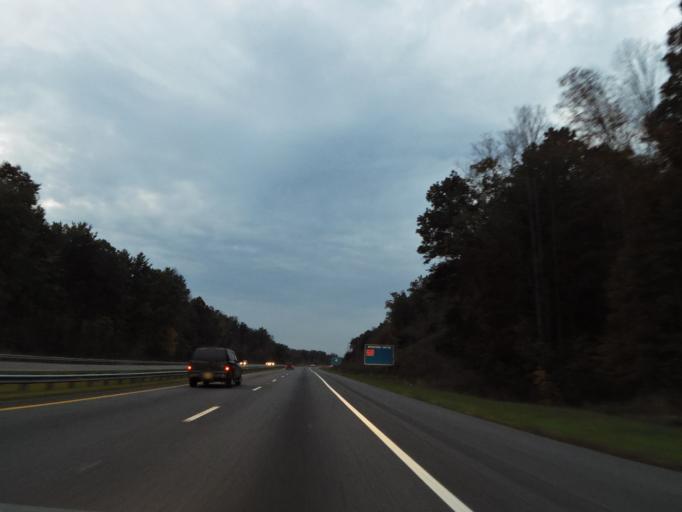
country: US
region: North Carolina
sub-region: McDowell County
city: Marion
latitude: 35.6885
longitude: -81.8990
